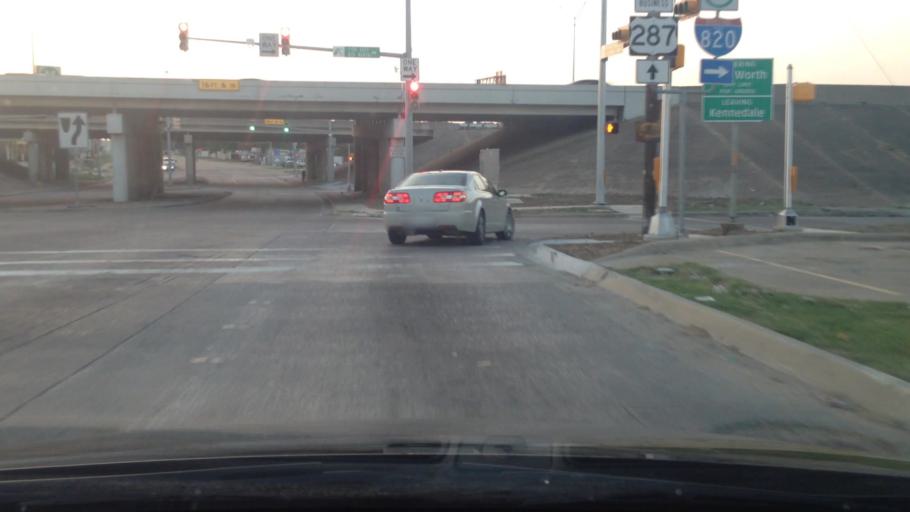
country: US
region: Texas
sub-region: Tarrant County
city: Kennedale
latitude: 32.6650
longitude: -97.2408
